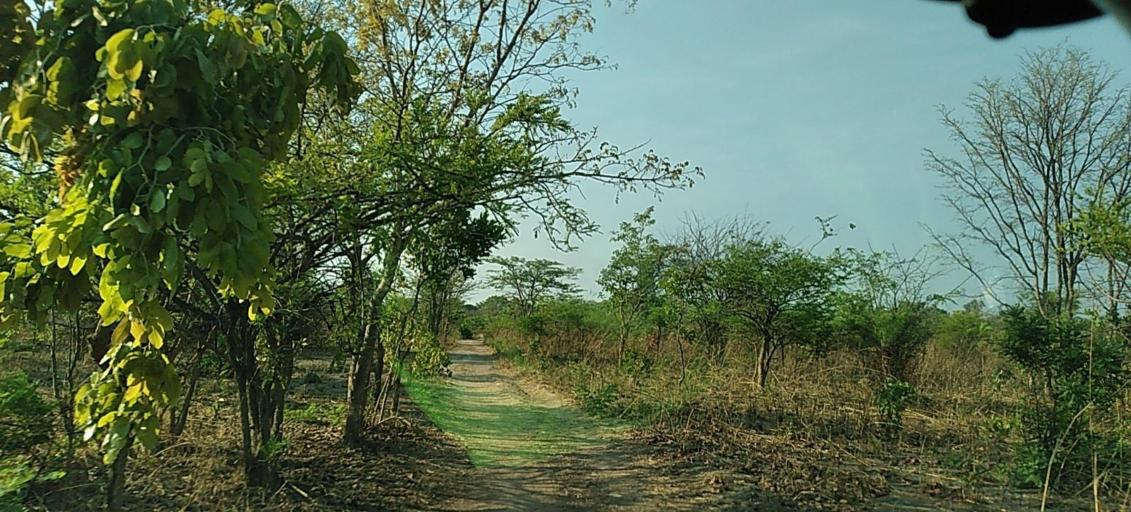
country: ZM
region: North-Western
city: Kalengwa
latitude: -13.1788
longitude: 25.0403
